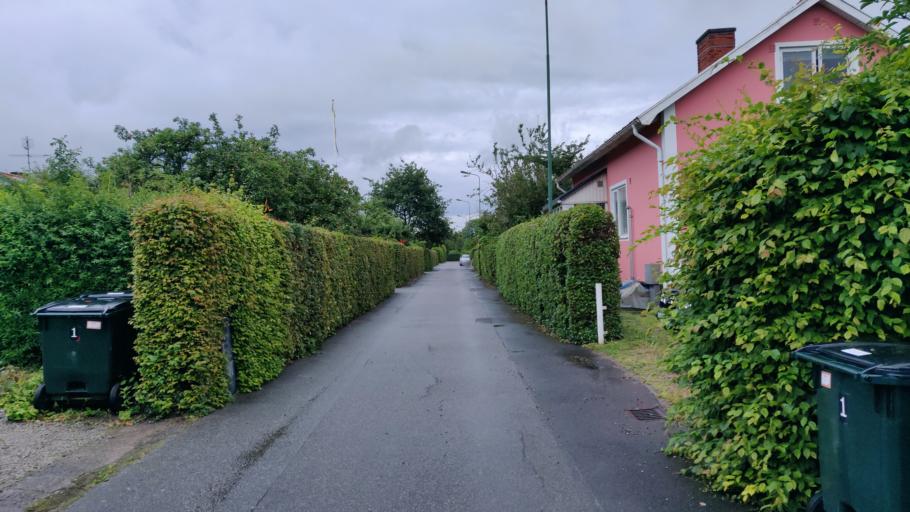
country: SE
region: Skane
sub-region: Lunds Kommun
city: Lund
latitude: 55.6983
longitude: 13.2213
